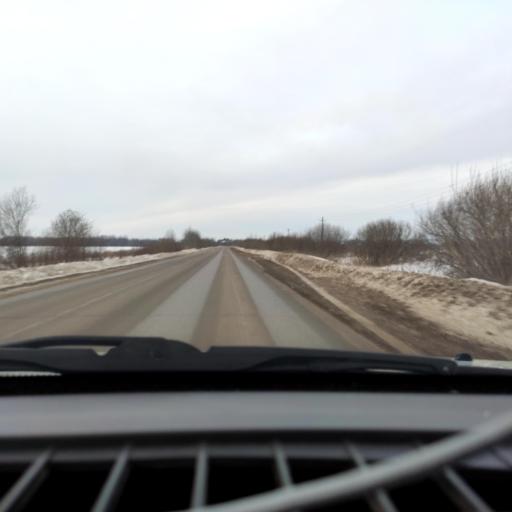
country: RU
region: Perm
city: Froly
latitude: 57.9034
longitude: 56.2822
